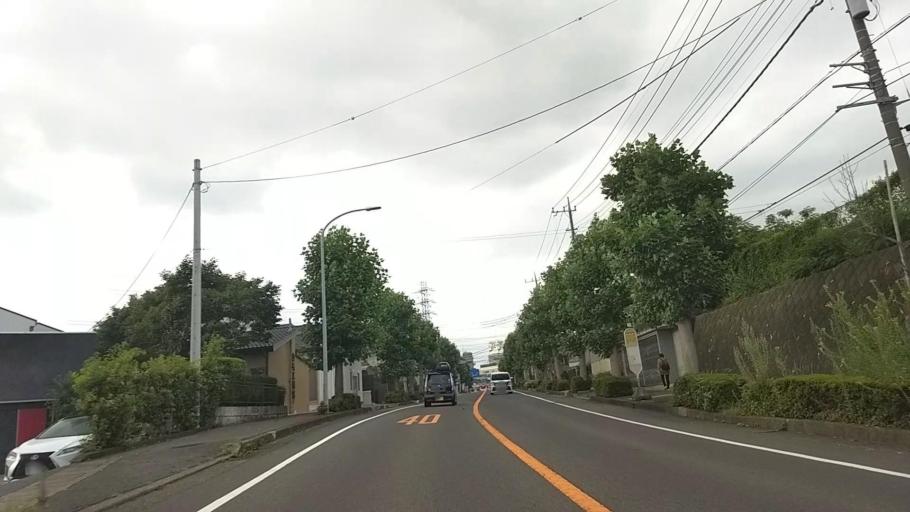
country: JP
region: Kanagawa
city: Isehara
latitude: 35.3903
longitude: 139.3145
